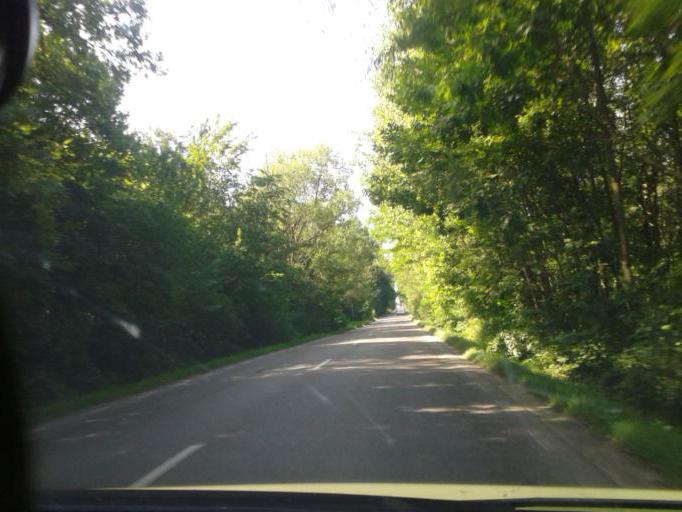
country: RO
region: Prahova
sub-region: Comuna Paulesti
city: Gageni
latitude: 45.0412
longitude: 25.9434
